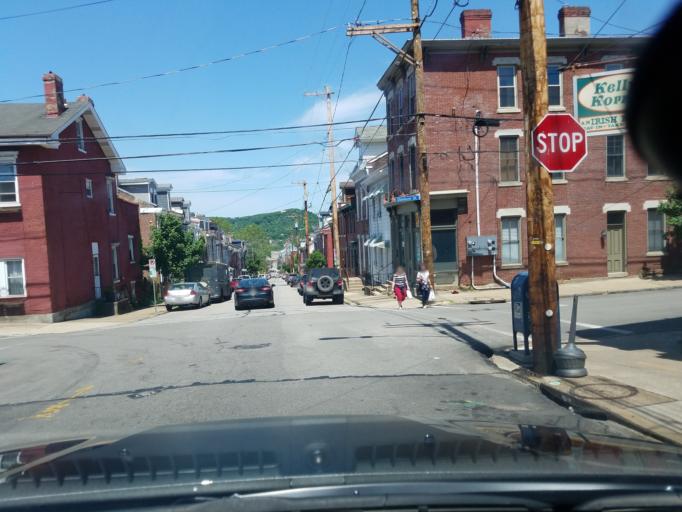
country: US
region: Pennsylvania
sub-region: Allegheny County
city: Bloomfield
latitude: 40.4705
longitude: -79.9568
